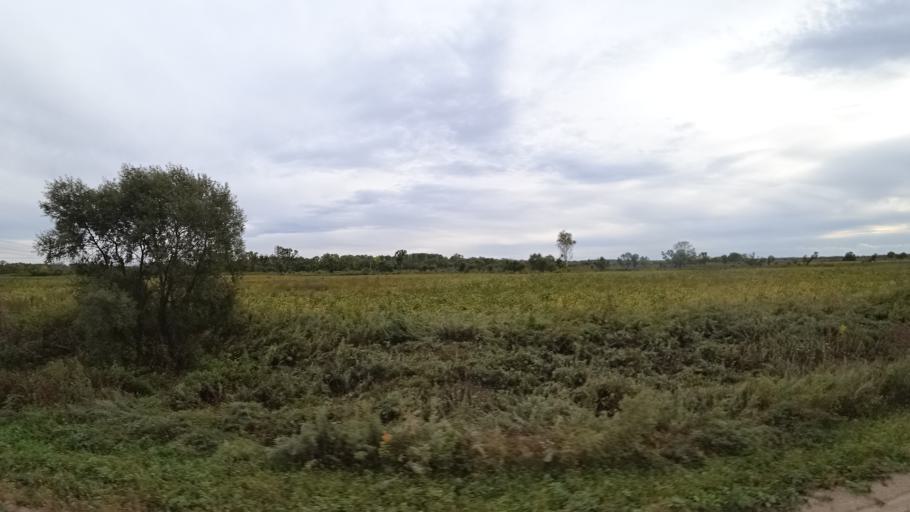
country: RU
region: Amur
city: Arkhara
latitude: 49.4298
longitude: 130.2489
